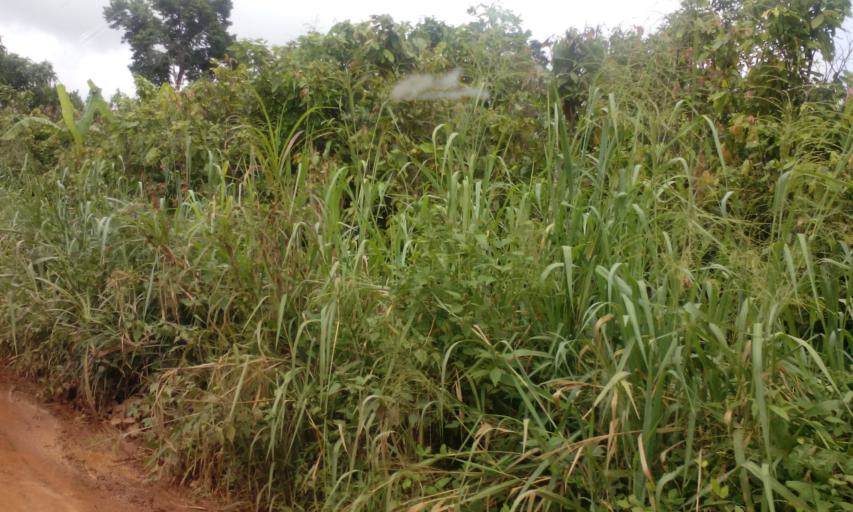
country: CI
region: Dix-Huit Montagnes
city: Man
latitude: 7.3202
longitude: -7.3779
